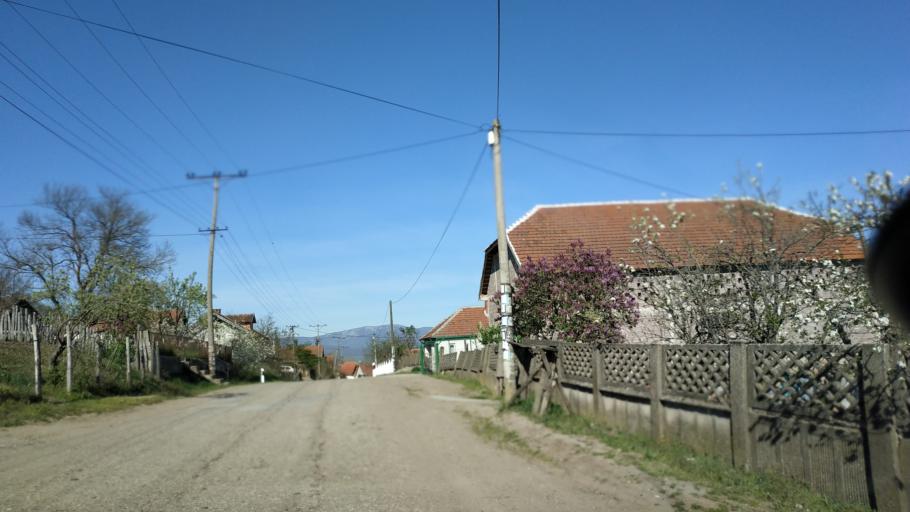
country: RS
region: Central Serbia
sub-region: Nisavski Okrug
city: Aleksinac
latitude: 43.4843
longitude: 21.6566
